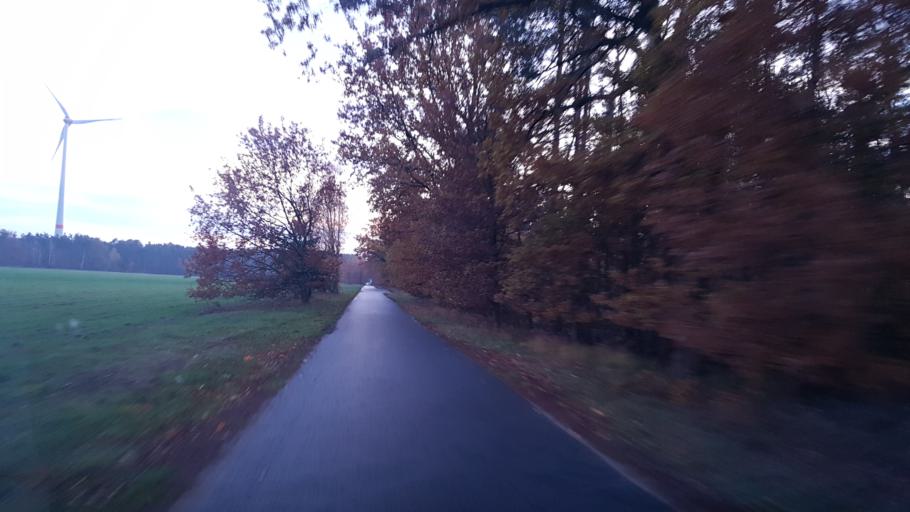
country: DE
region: Brandenburg
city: Herzberg
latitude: 51.6426
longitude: 13.2151
